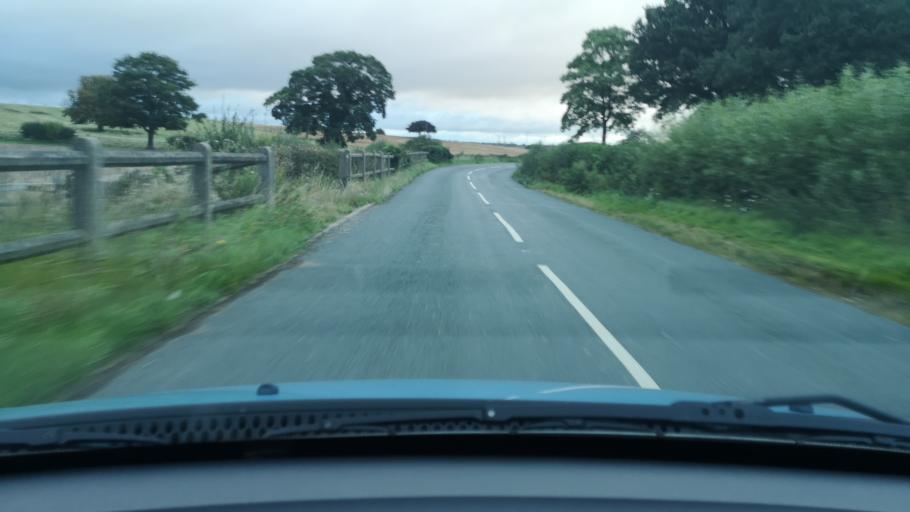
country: GB
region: England
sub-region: City and Borough of Wakefield
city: Badsworth
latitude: 53.6286
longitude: -1.2956
